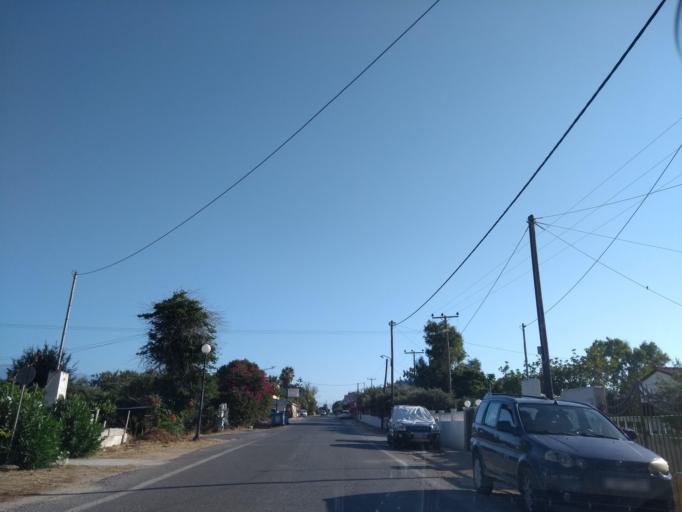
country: GR
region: Crete
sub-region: Nomos Chanias
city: Pithari
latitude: 35.5871
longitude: 24.0925
